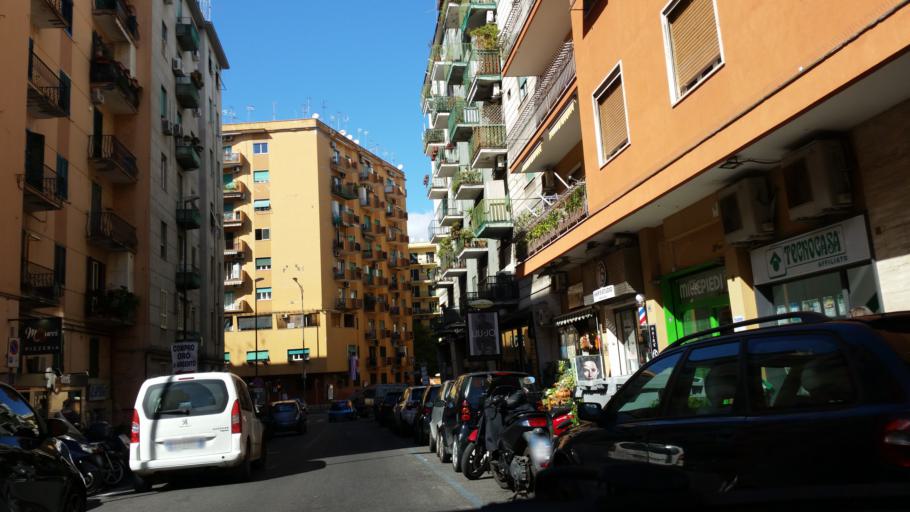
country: IT
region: Campania
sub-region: Provincia di Napoli
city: Napoli
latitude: 40.8425
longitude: 14.2218
